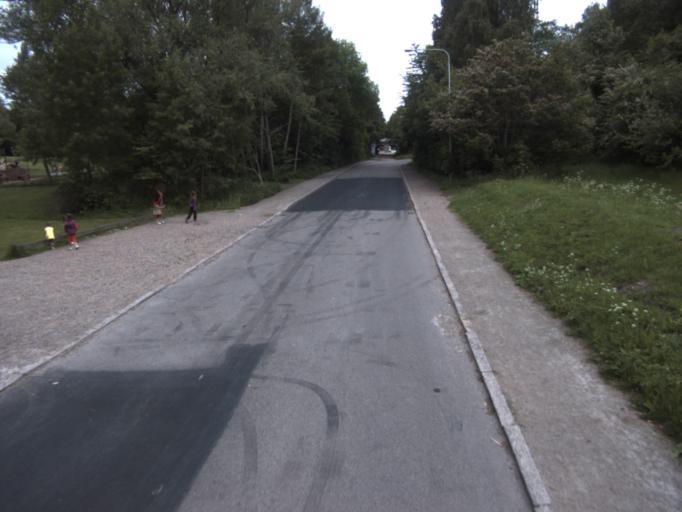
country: SE
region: Skane
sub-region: Helsingborg
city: Helsingborg
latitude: 56.0359
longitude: 12.7287
